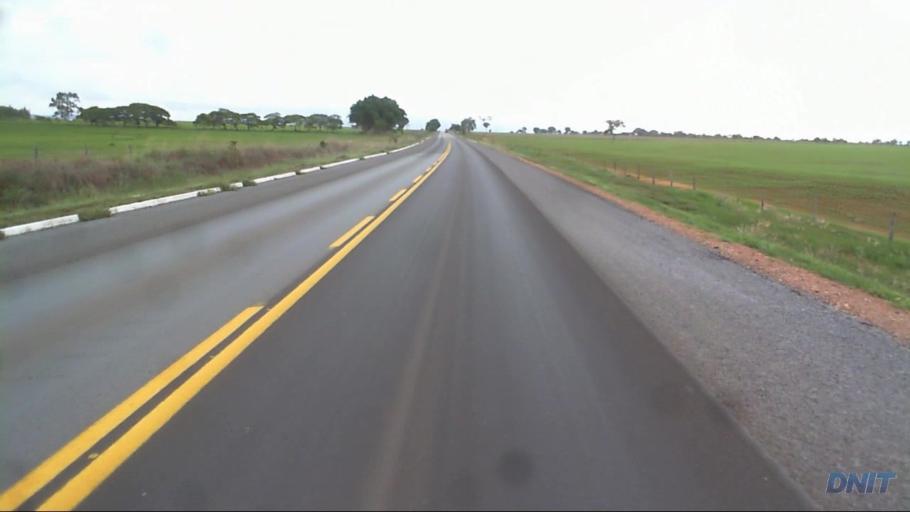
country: BR
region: Goias
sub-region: Padre Bernardo
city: Padre Bernardo
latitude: -15.2188
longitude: -48.6239
